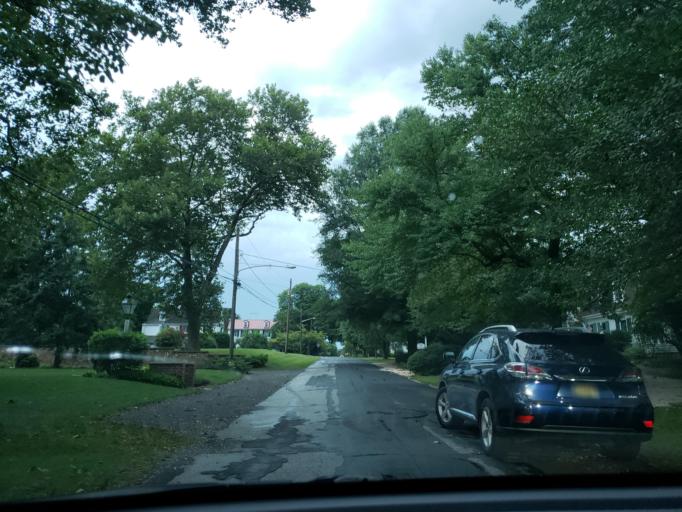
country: US
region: Delaware
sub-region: New Castle County
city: Middletown
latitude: 39.4551
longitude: -75.6563
